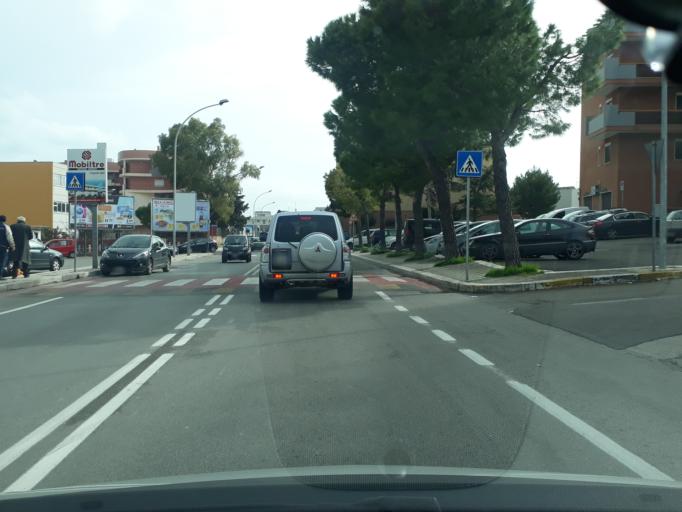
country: IT
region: Apulia
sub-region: Provincia di Bari
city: Monopoli
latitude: 40.9497
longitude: 17.2889
